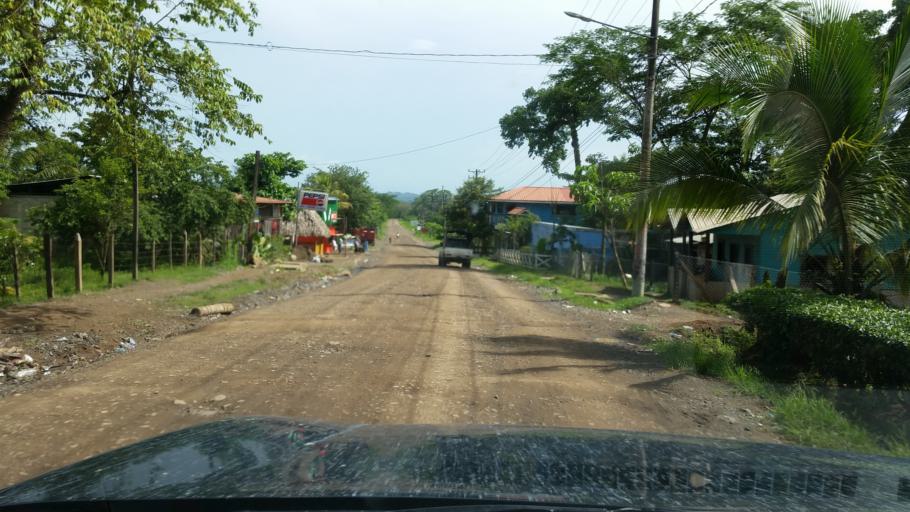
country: NI
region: Atlantico Norte (RAAN)
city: Siuna
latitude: 13.7130
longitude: -84.7747
